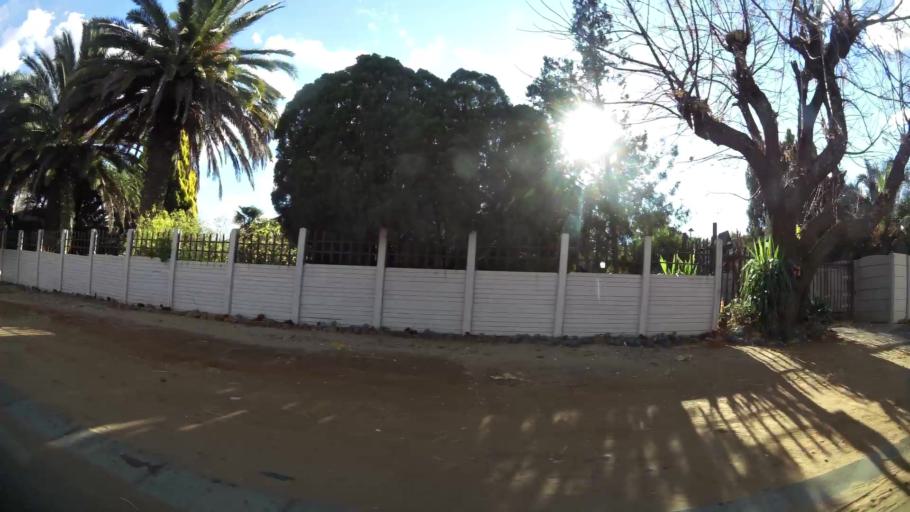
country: ZA
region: North-West
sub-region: Dr Kenneth Kaunda District Municipality
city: Klerksdorp
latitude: -26.8404
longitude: 26.6577
